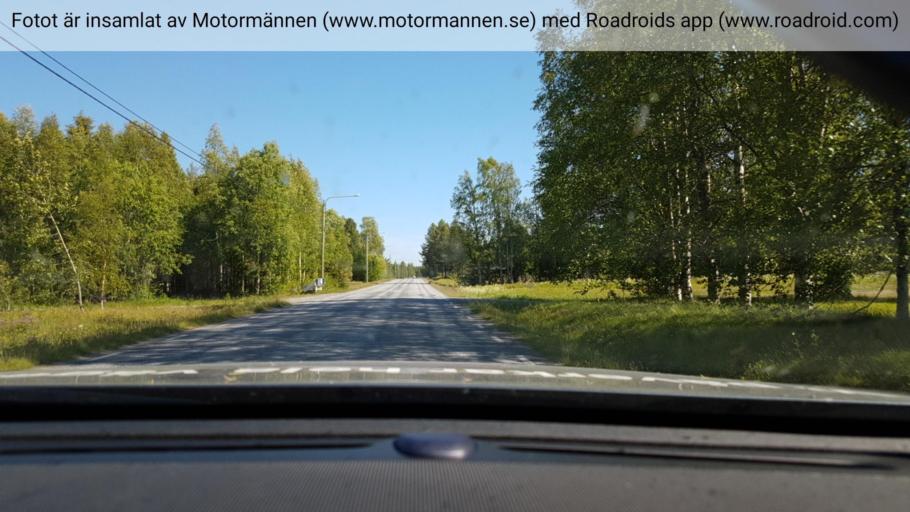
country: SE
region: Vaesterbotten
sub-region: Vilhelmina Kommun
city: Sjoberg
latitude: 64.6493
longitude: 16.3375
